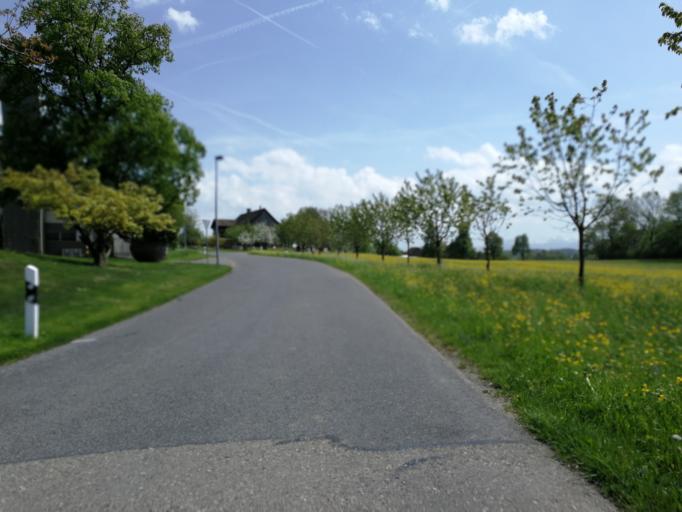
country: CH
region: Zurich
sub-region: Bezirk Hinwil
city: Gossau
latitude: 47.2981
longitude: 8.7647
